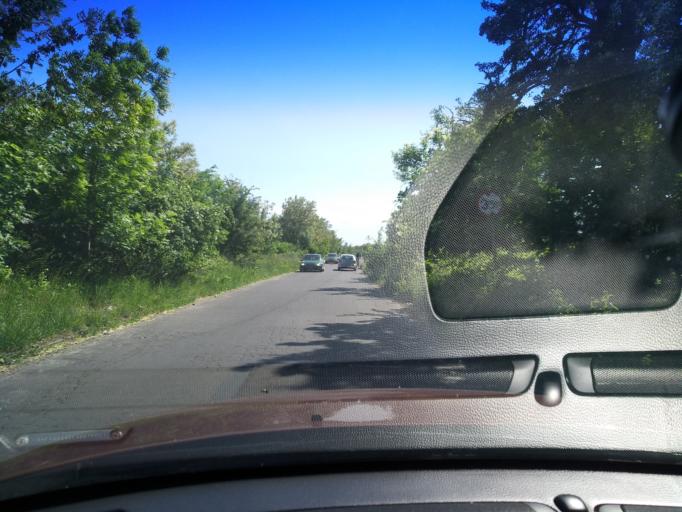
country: PL
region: Lower Silesian Voivodeship
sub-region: Powiat zgorzelecki
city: Zgorzelec
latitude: 51.1515
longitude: 15.0196
